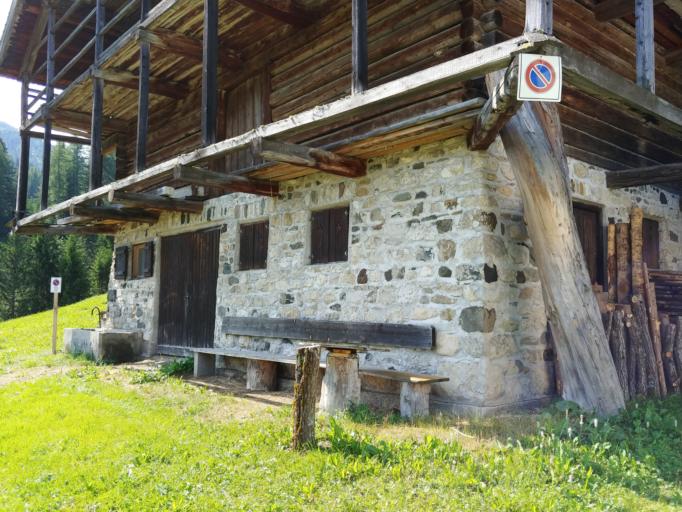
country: IT
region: Trentino-Alto Adige
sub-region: Bolzano
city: Santa Cristina Valgardena
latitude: 46.5527
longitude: 11.7242
